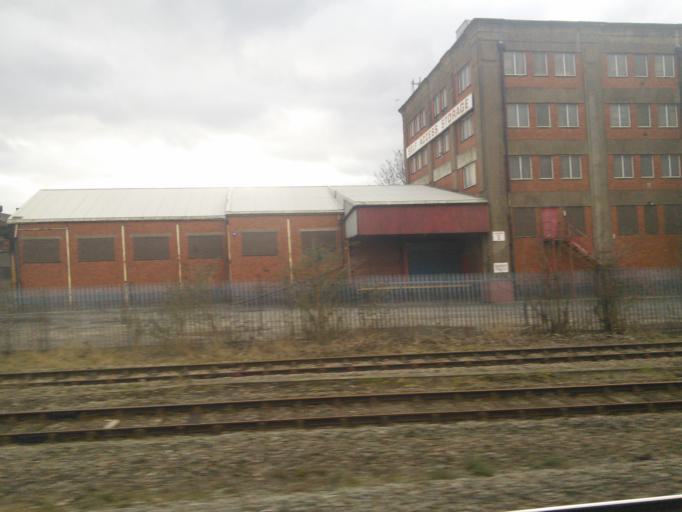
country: GB
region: England
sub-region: City and Borough of Birmingham
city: Birmingham
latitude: 52.4692
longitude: -1.8733
